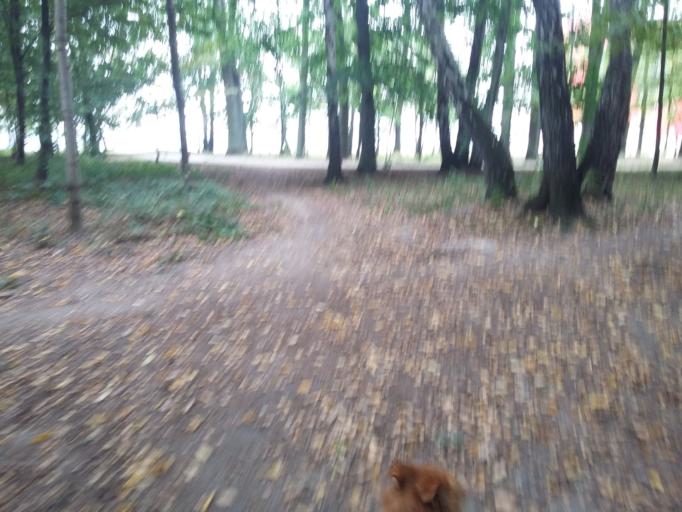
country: PL
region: Lodz Voivodeship
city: Lodz
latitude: 51.7601
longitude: 19.4235
